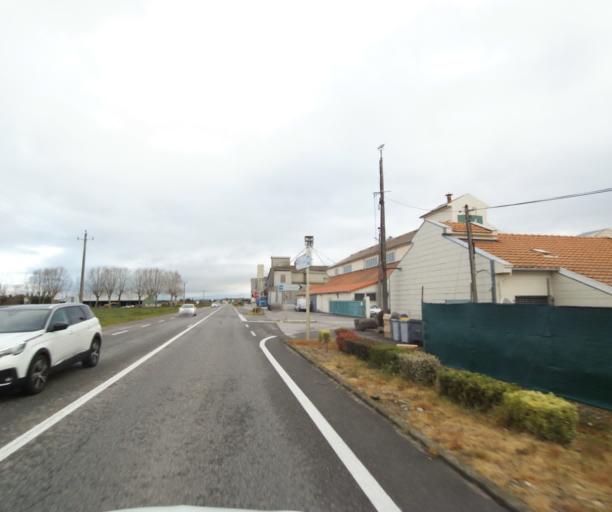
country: FR
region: Midi-Pyrenees
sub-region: Departement de l'Ariege
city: Saverdun
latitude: 43.1967
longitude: 1.6100
